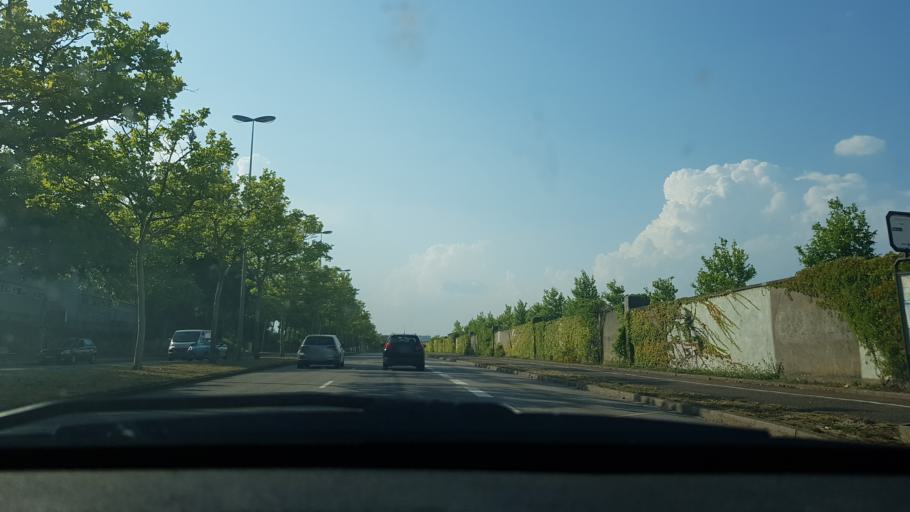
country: FR
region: Lorraine
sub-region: Departement de Meurthe-et-Moselle
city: Nancy
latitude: 48.6700
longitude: 6.1881
